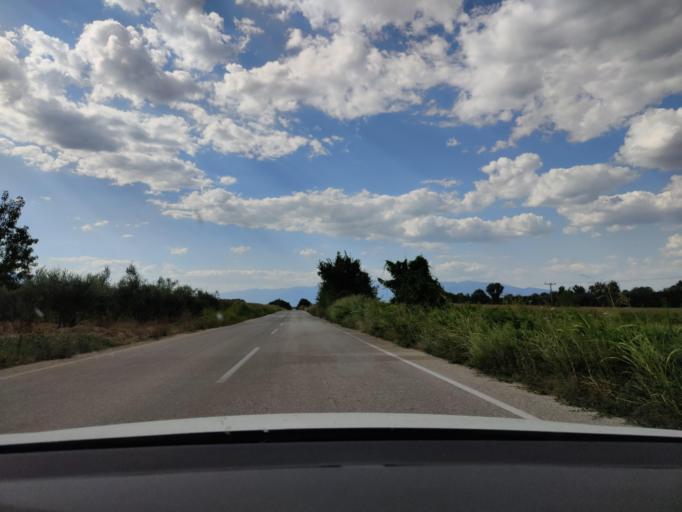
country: GR
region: Central Macedonia
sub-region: Nomos Serron
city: Strymoniko
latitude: 41.0650
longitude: 23.3068
